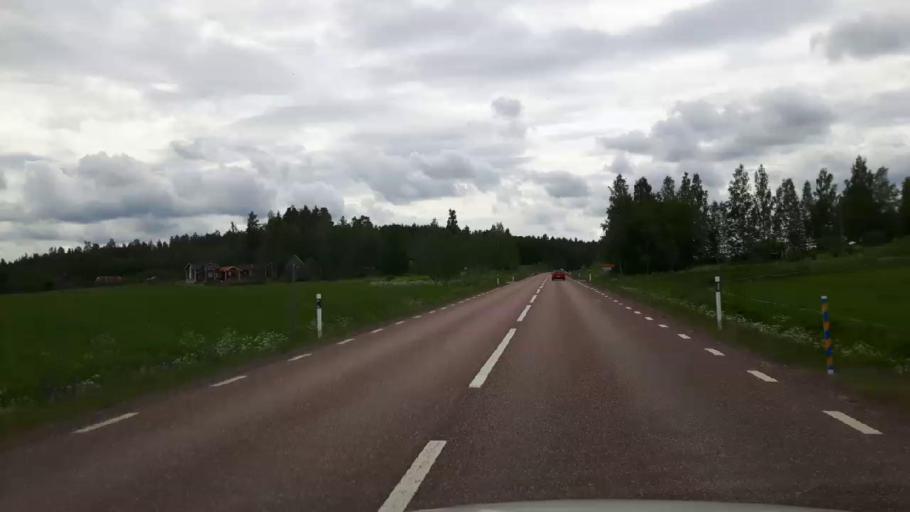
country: SE
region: Dalarna
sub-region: Hedemora Kommun
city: Brunna
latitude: 60.2288
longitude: 15.9988
